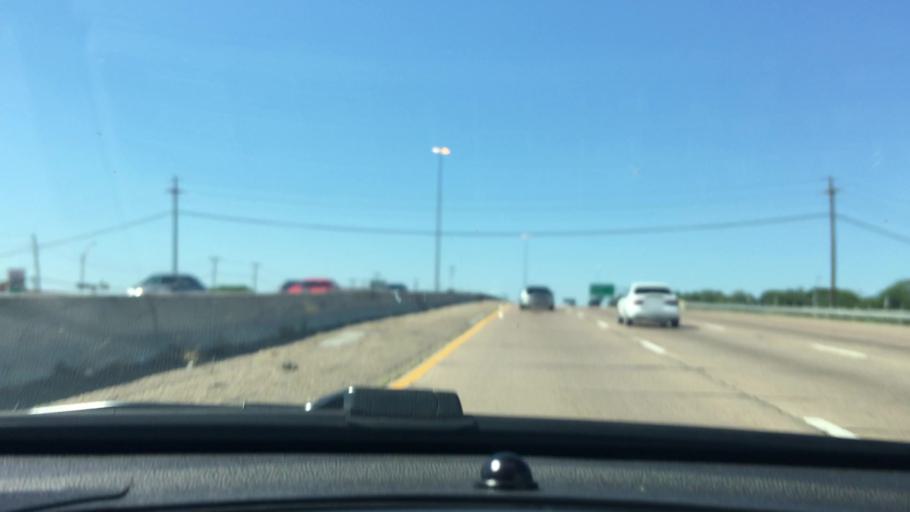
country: US
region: Texas
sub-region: Dallas County
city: Cockrell Hill
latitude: 32.6905
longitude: -96.8231
